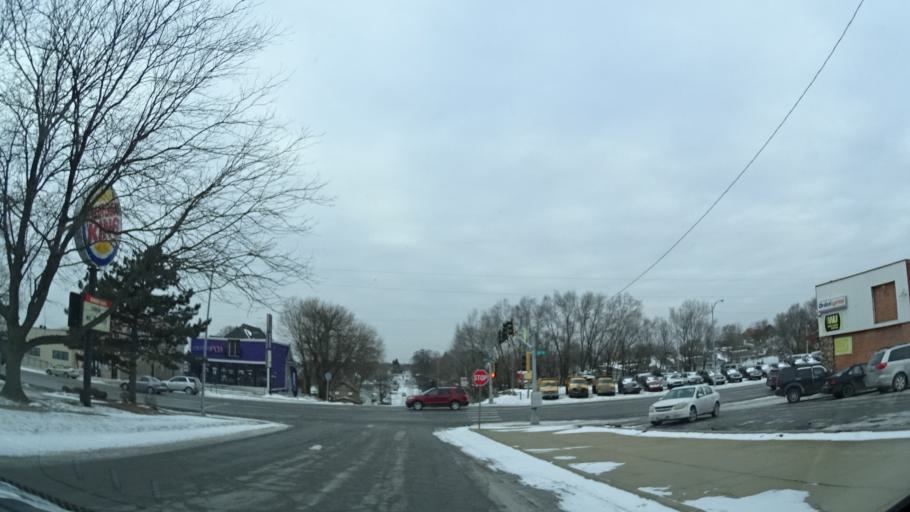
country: US
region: Nebraska
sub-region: Douglas County
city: Omaha
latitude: 41.2173
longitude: -95.9465
